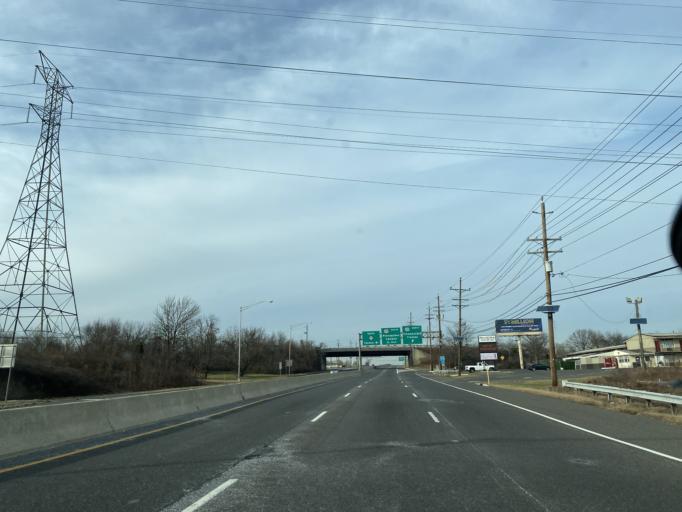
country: US
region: New Jersey
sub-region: Burlington County
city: Cinnaminson
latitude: 39.9798
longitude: -75.0141
